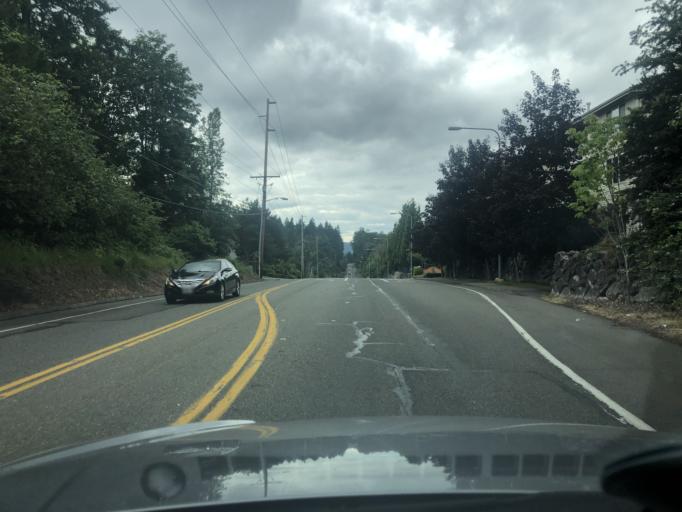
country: US
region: Washington
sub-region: King County
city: Lea Hill
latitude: 47.3225
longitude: -122.1787
